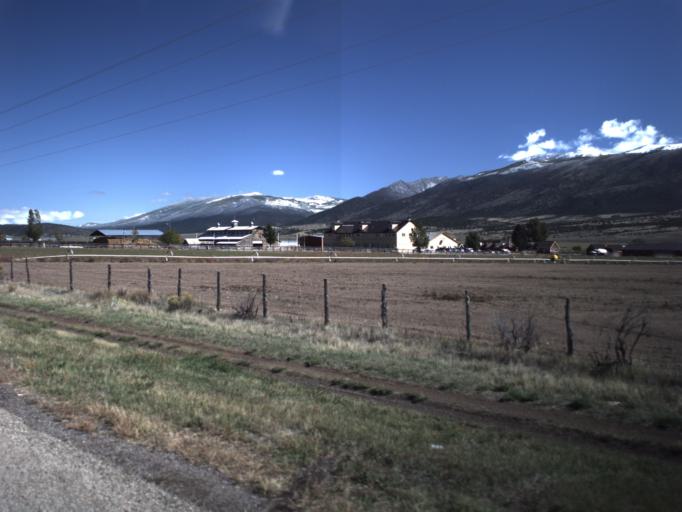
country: US
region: Utah
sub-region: Wayne County
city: Loa
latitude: 38.5150
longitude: -111.8814
